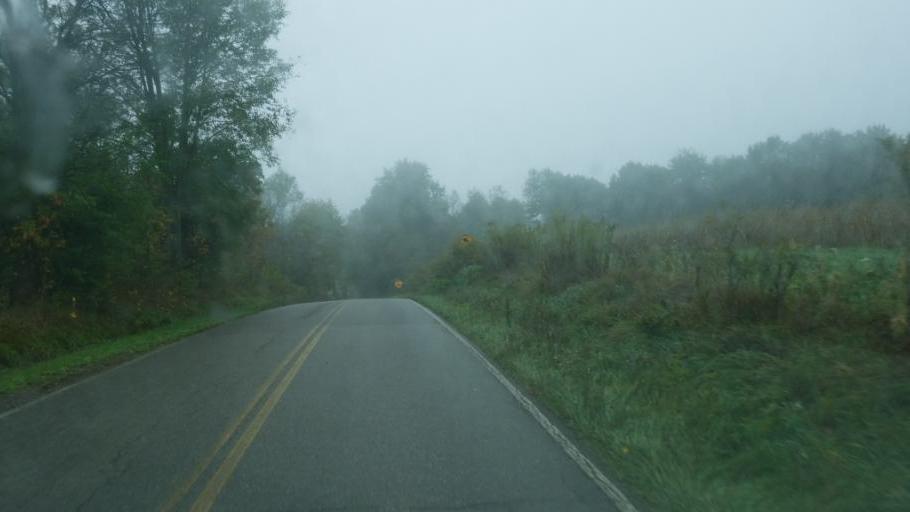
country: US
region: Ohio
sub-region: Harrison County
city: Cadiz
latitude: 40.3734
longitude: -81.0995
